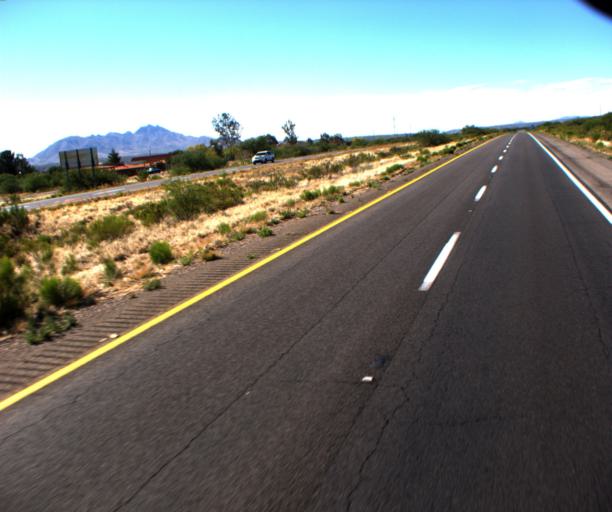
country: US
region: Arizona
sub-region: Santa Cruz County
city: Tubac
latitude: 31.6212
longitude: -111.0542
